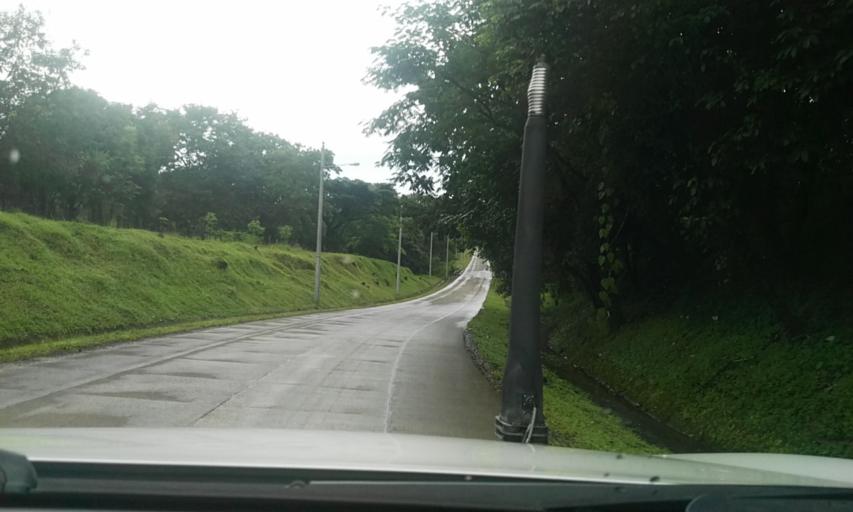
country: NI
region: Matagalpa
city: Rio Blanco
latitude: 12.9246
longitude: -85.1905
